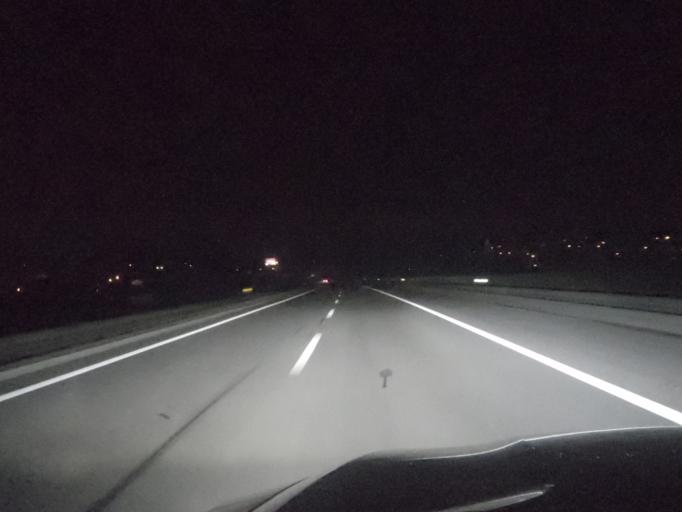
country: PT
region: Aveiro
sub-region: Aveiro
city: Eixo
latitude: 40.6206
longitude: -8.5386
